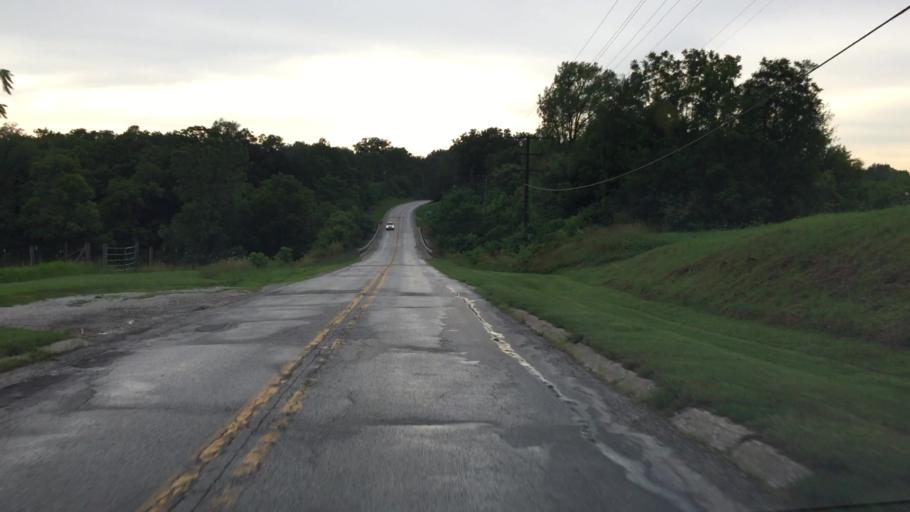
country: US
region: Illinois
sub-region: Hancock County
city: Warsaw
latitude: 40.3566
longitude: -91.4226
